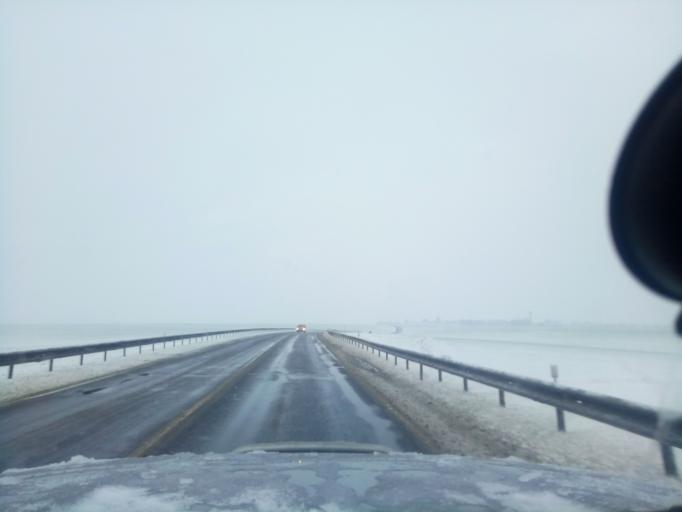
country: BY
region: Minsk
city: Haradzyeya
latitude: 53.3292
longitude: 26.5493
